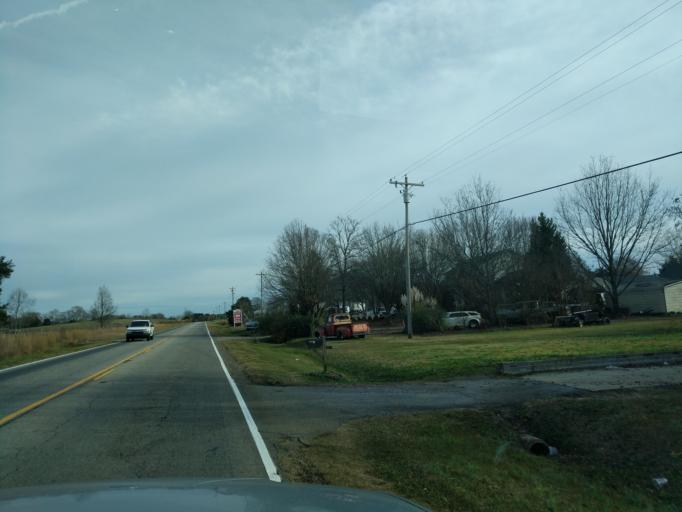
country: US
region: South Carolina
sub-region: Pickens County
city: Liberty
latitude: 34.7132
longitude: -82.6073
